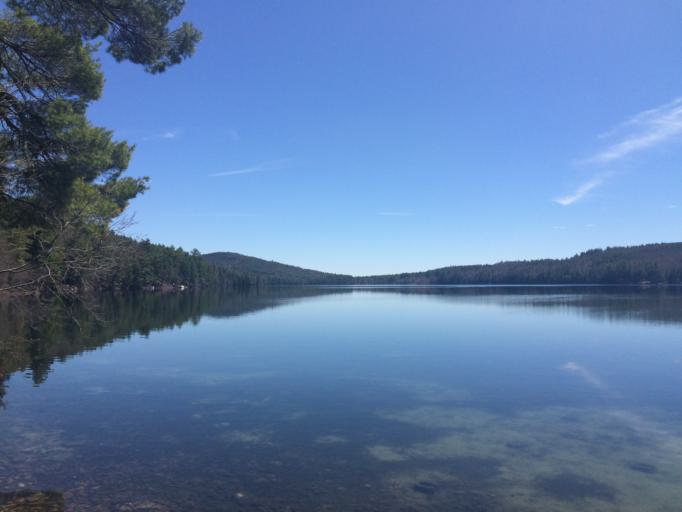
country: US
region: Maine
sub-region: Oxford County
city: Porter
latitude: 43.7653
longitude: -70.8663
